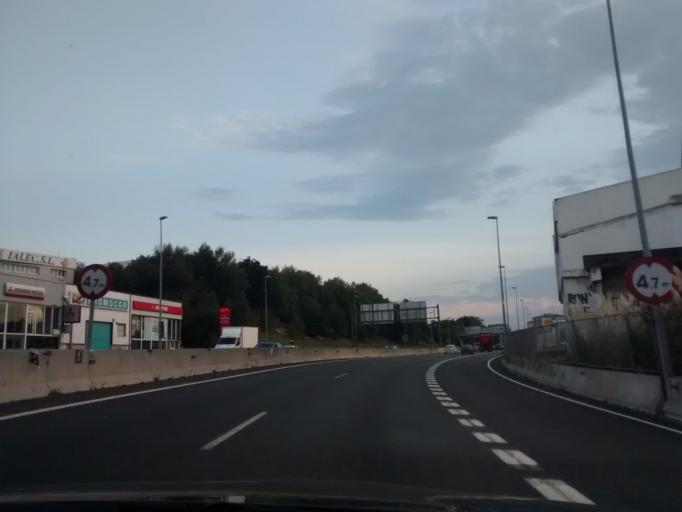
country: ES
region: Cantabria
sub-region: Provincia de Cantabria
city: El Astillero
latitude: 43.4228
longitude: -3.8355
